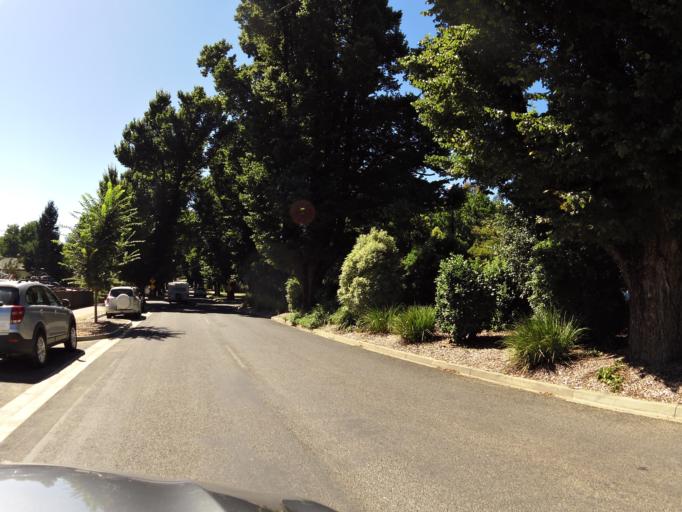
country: AU
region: Victoria
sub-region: Alpine
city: Mount Beauty
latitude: -36.7302
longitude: 146.9614
